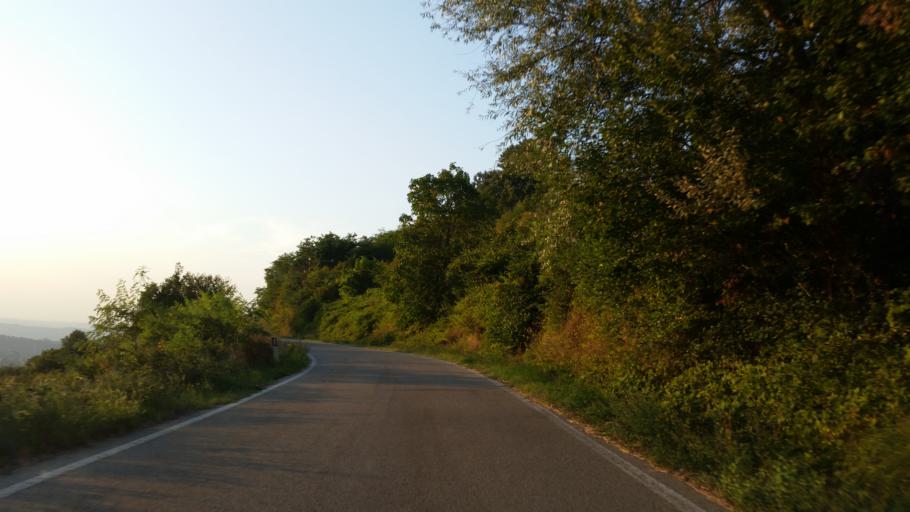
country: IT
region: Piedmont
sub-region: Provincia di Cuneo
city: Mango
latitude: 44.6585
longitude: 8.1349
